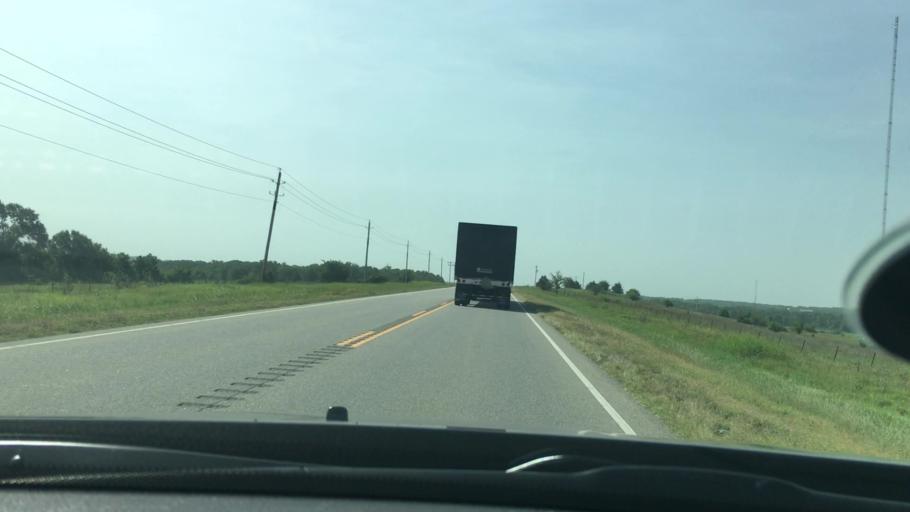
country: US
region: Oklahoma
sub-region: Atoka County
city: Atoka
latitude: 34.4223
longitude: -96.1913
